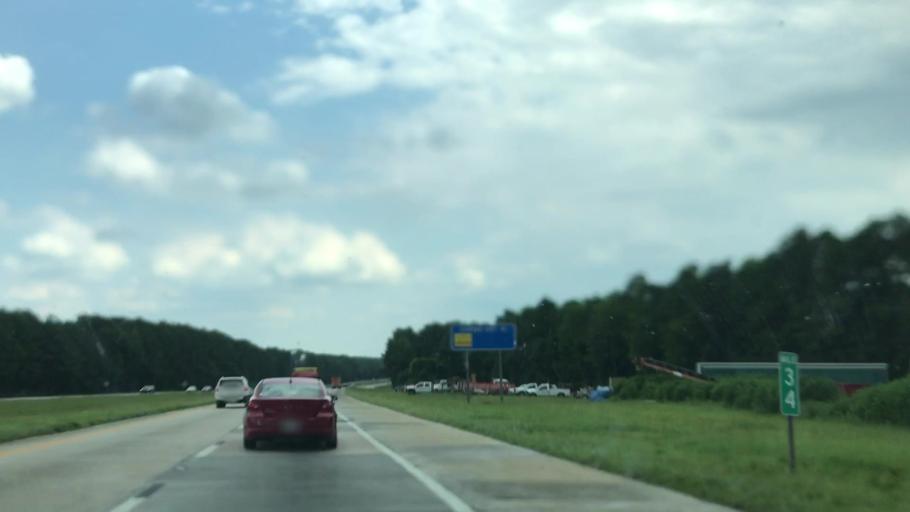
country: US
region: South Carolina
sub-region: Richland County
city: Blythewood
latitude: 34.3071
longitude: -80.9998
